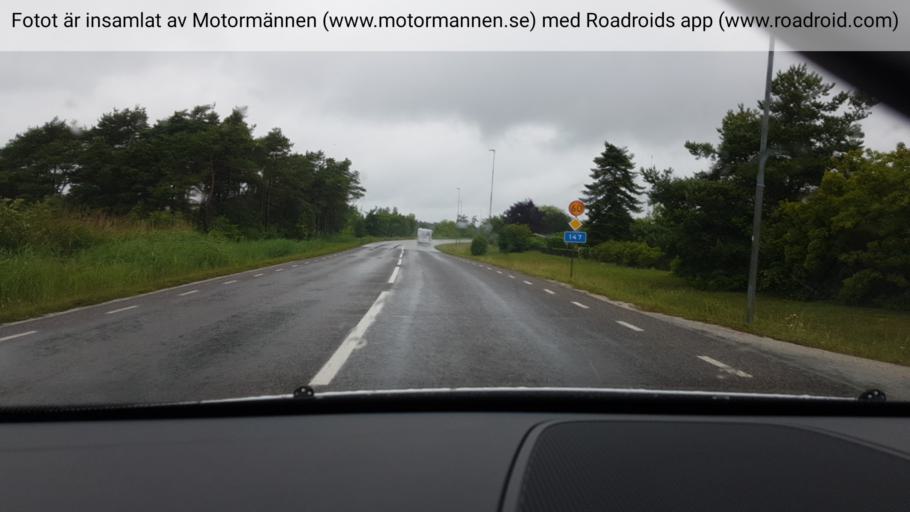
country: SE
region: Gotland
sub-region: Gotland
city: Slite
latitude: 57.6966
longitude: 18.7978
